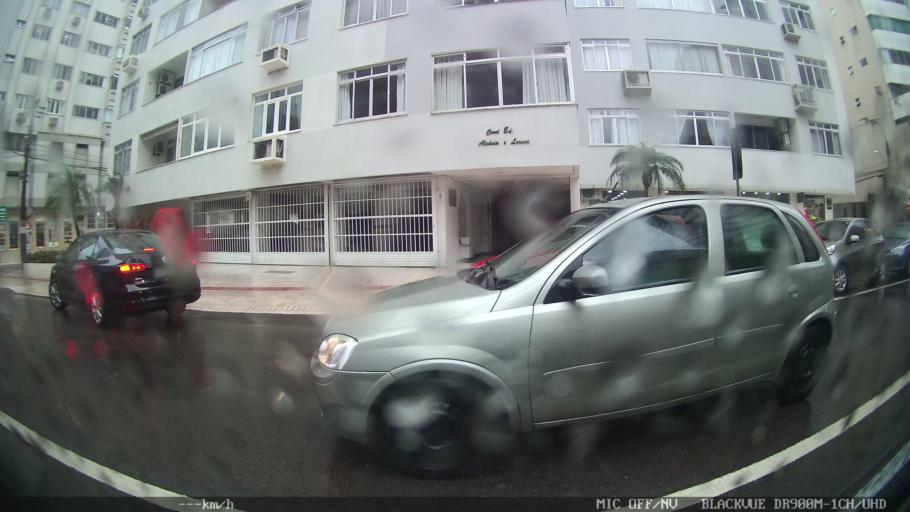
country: BR
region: Santa Catarina
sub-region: Balneario Camboriu
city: Balneario Camboriu
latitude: -26.9806
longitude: -48.6366
